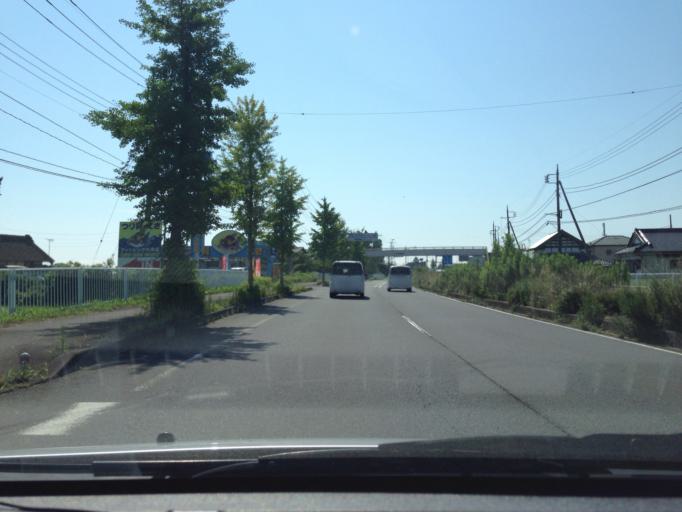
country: JP
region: Ibaraki
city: Oarai
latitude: 36.3349
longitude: 140.5516
